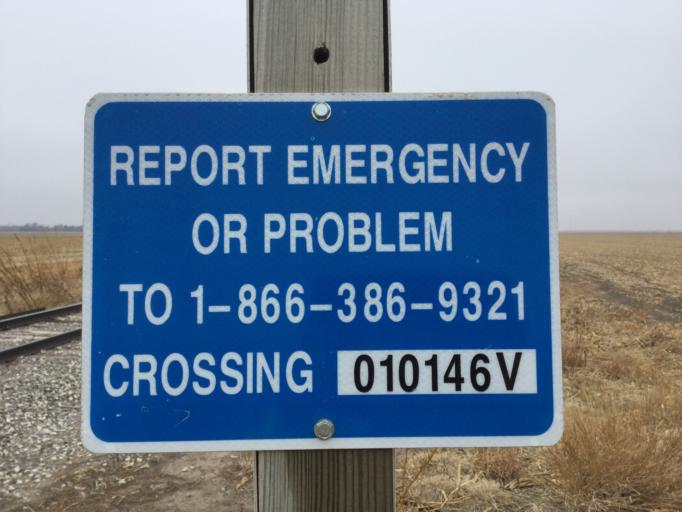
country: US
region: Kansas
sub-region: Edwards County
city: Kinsley
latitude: 38.1958
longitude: -99.4242
